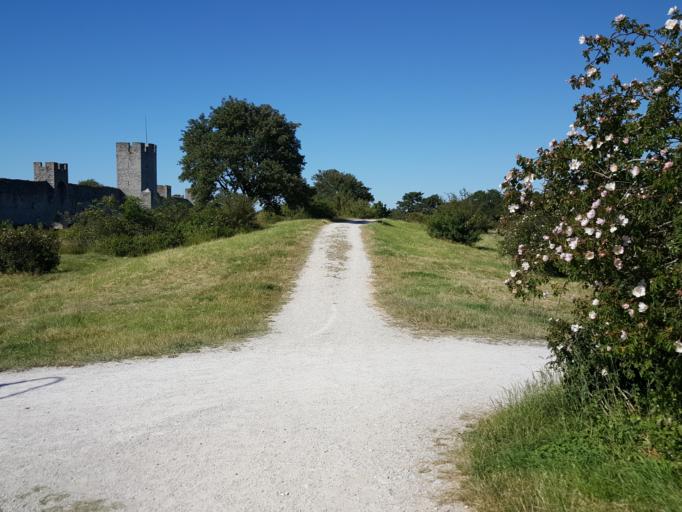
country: SE
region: Gotland
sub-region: Gotland
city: Visby
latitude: 57.6415
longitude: 18.3013
